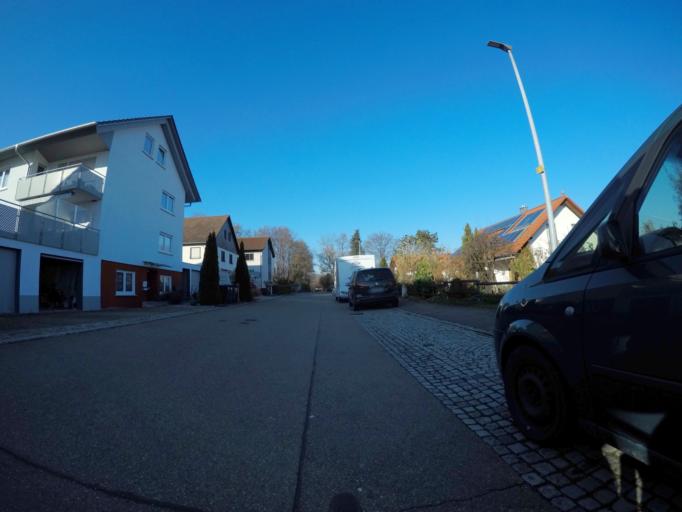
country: DE
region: Baden-Wuerttemberg
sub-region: Tuebingen Region
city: Reutlingen
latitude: 48.5205
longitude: 9.2248
